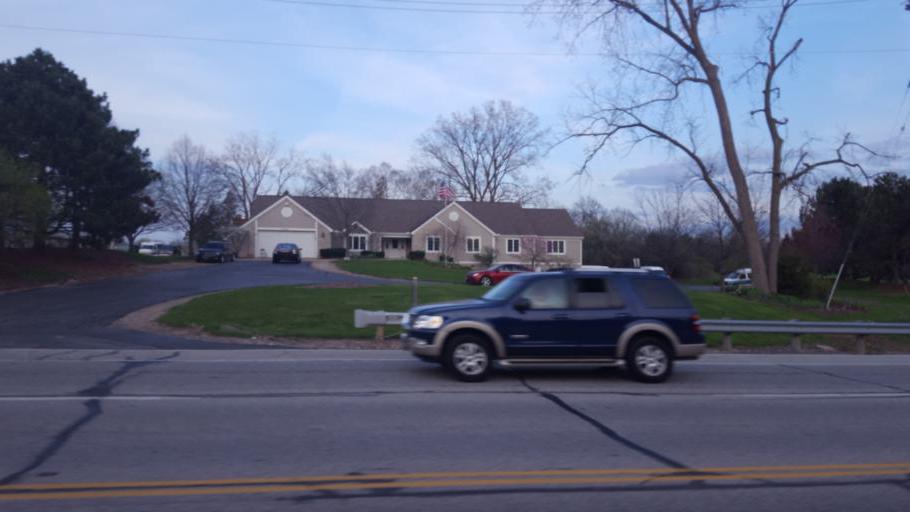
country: US
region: Ohio
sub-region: Lorain County
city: Lorain
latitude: 41.4407
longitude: -82.2026
